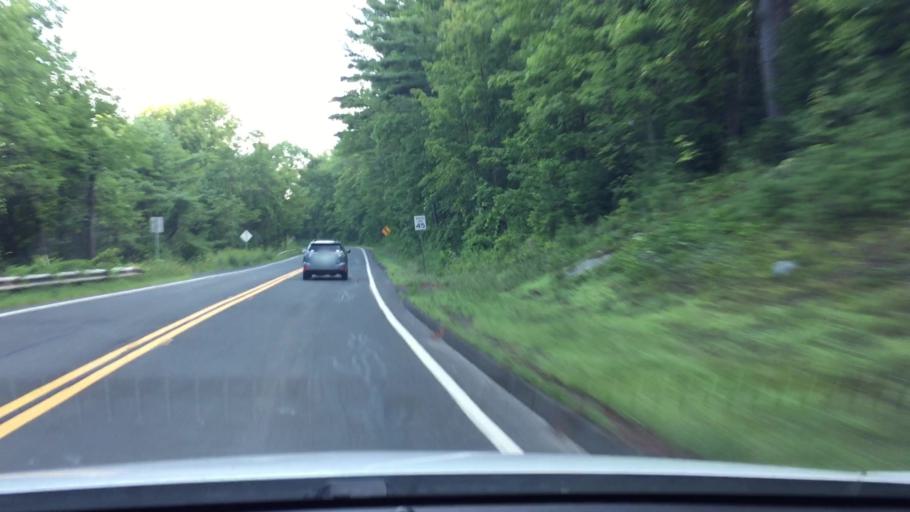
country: US
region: Massachusetts
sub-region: Berkshire County
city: Otis
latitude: 42.2258
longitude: -73.1074
